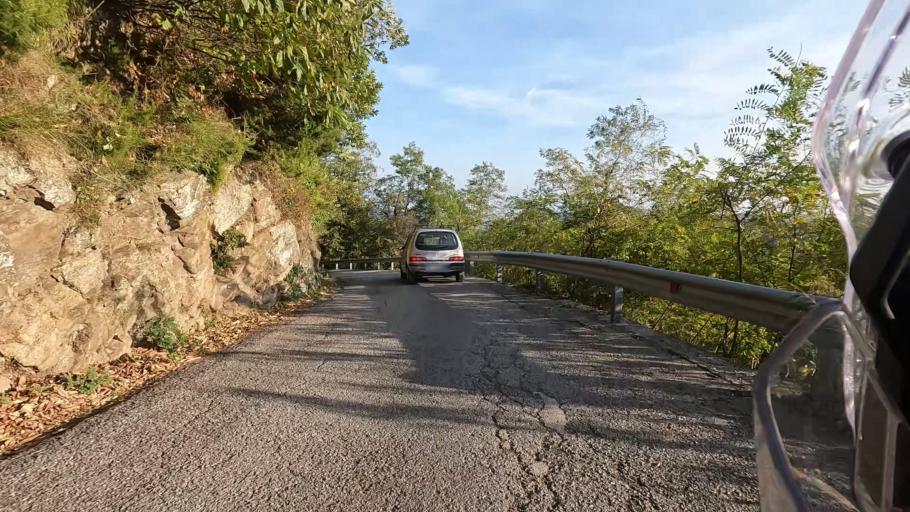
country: IT
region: Liguria
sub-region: Provincia di Savona
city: San Giovanni
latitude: 44.4080
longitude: 8.5224
